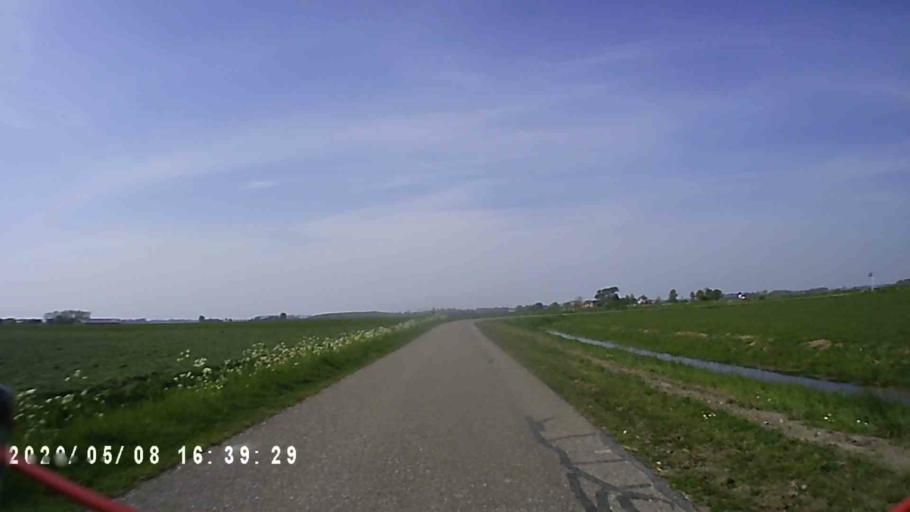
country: NL
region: Groningen
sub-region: Gemeente Bedum
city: Bedum
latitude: 53.3667
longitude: 6.6057
